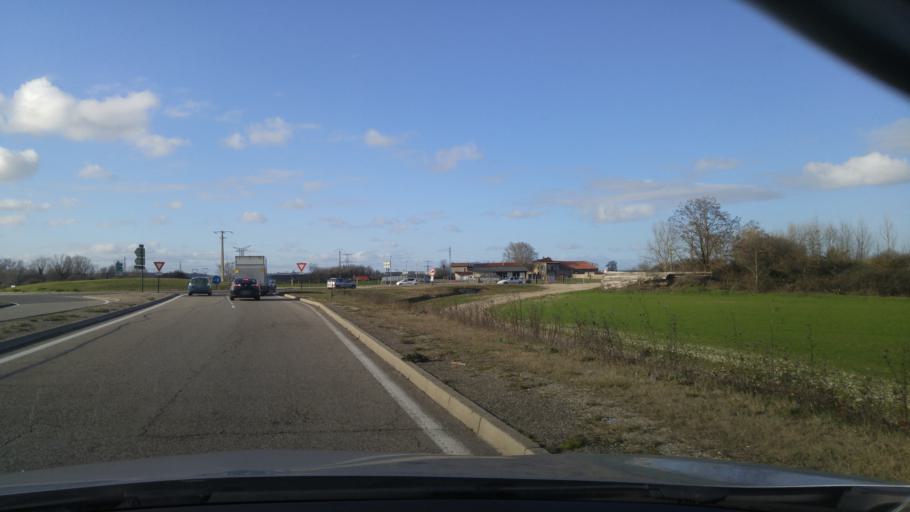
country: FR
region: Rhone-Alpes
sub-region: Departement de l'Isere
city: La Verpilliere
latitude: 45.6495
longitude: 5.1380
